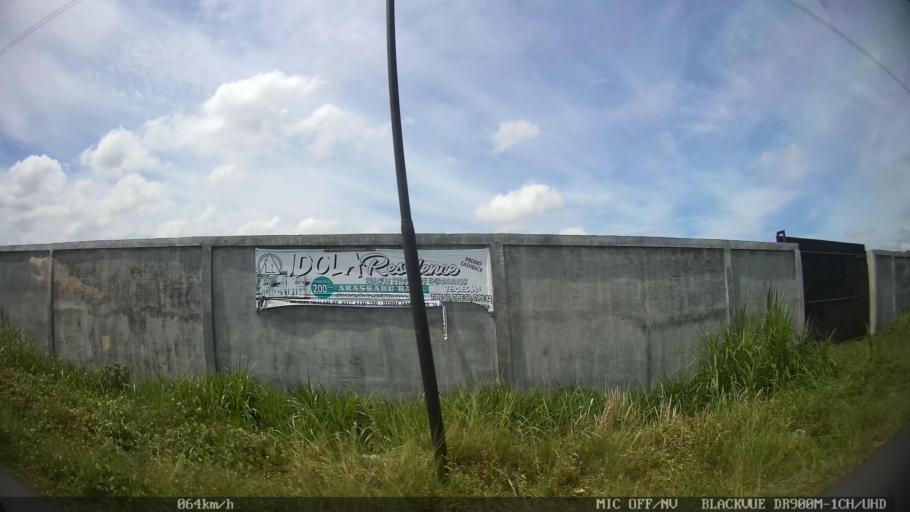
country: ID
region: North Sumatra
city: Percut
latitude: 3.5892
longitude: 98.8776
